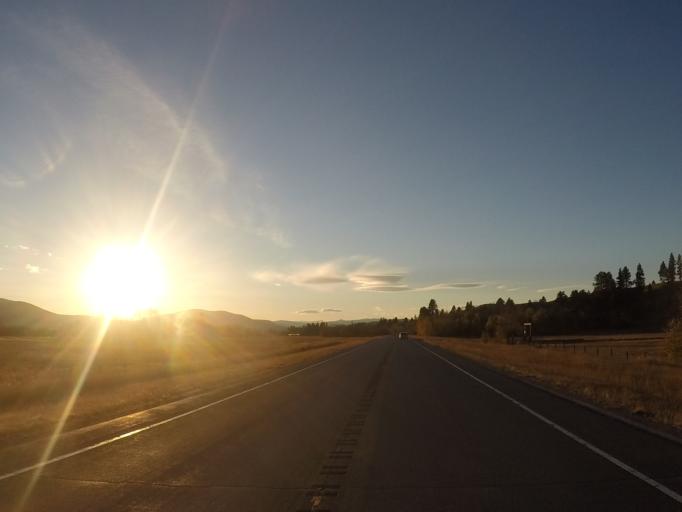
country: US
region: Montana
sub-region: Lewis and Clark County
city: Lincoln
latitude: 47.0164
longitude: -113.0752
